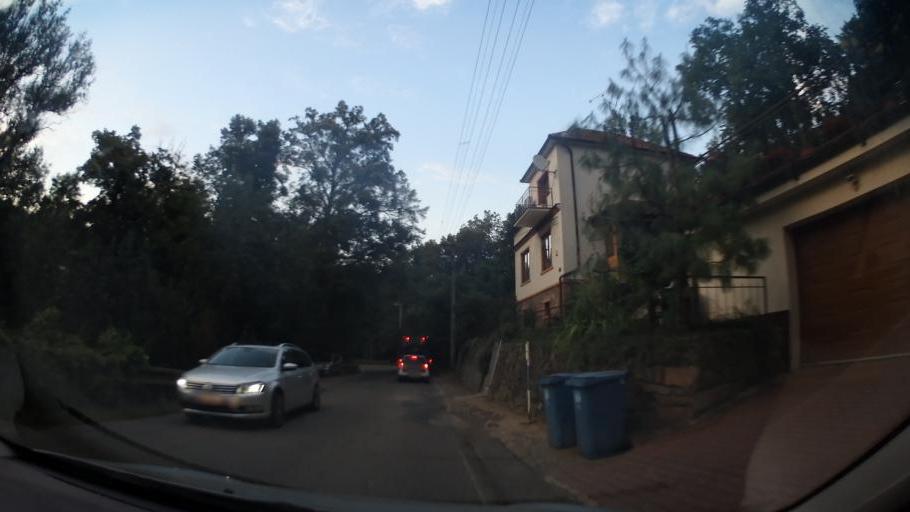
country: CZ
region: South Moravian
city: Dolni Kounice
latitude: 49.0724
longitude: 16.4722
